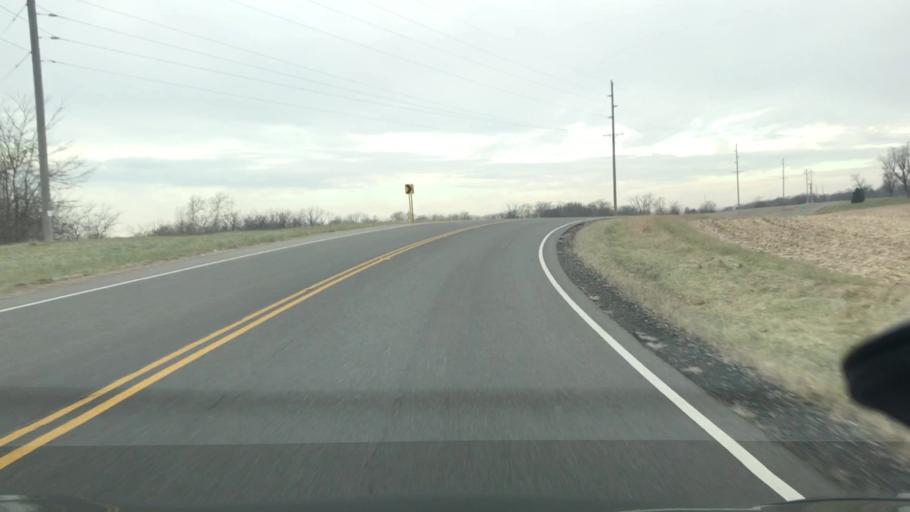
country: US
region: Ohio
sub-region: Madison County
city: London
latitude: 39.8585
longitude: -83.4082
